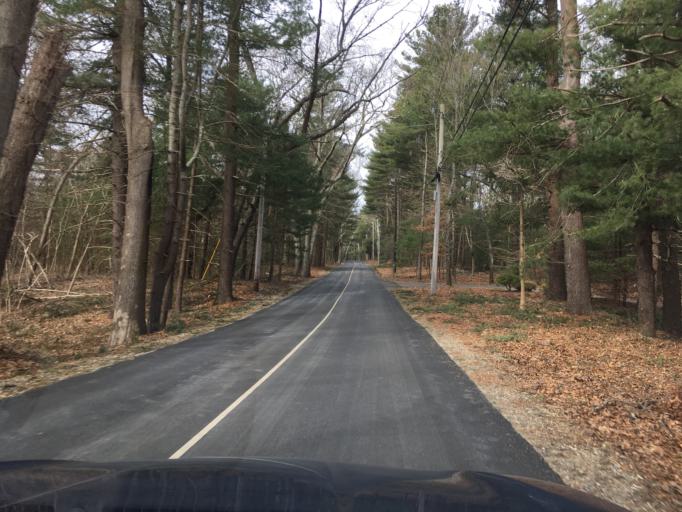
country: US
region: Rhode Island
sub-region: Kent County
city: East Greenwich
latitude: 41.6485
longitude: -71.4289
